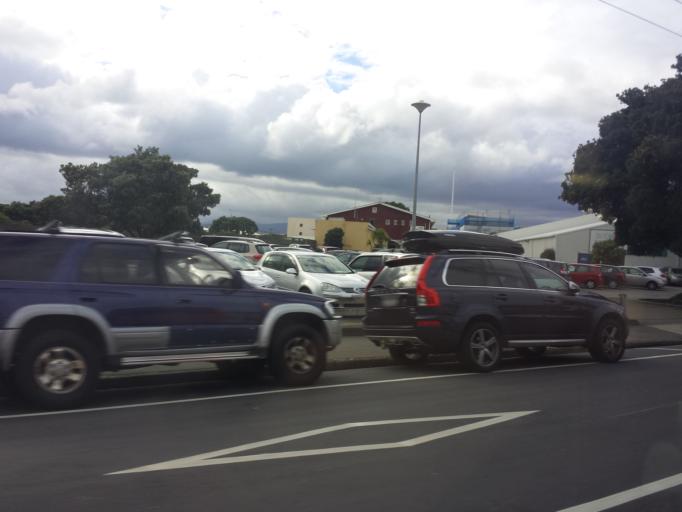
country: NZ
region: Wellington
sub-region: Wellington City
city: Wellington
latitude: -41.3159
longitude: 174.7937
